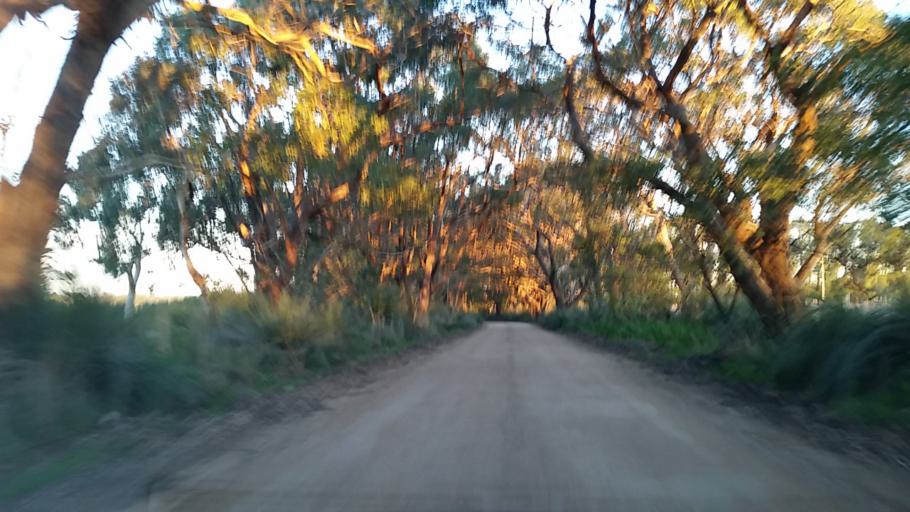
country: AU
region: South Australia
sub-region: Alexandrina
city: Mount Compass
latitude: -35.2841
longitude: 138.5998
